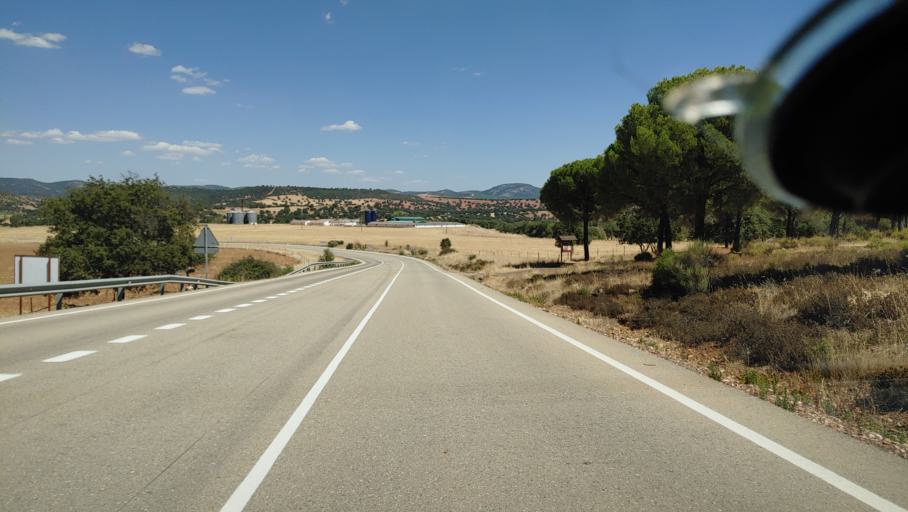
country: ES
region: Castille-La Mancha
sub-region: Provincia de Ciudad Real
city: Saceruela
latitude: 39.0111
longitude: -4.4989
